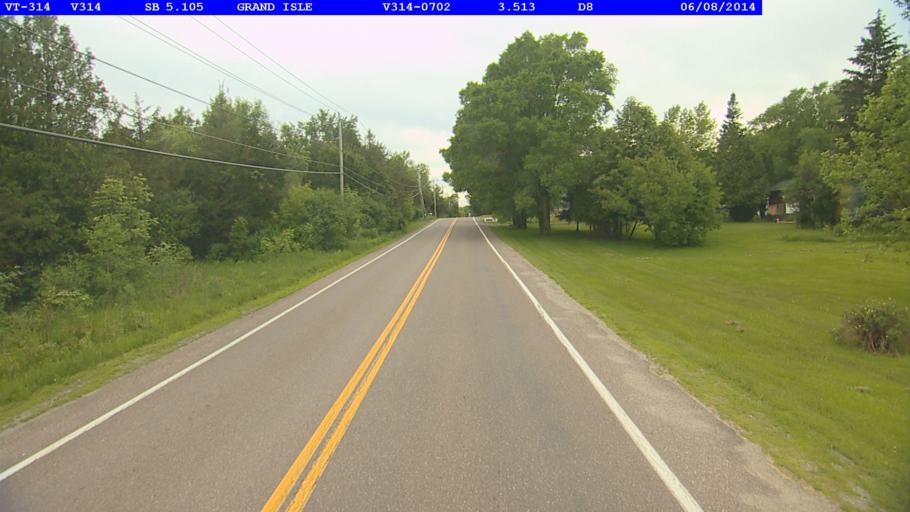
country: US
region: New York
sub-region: Clinton County
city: Cumberland Head
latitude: 44.7025
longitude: -73.3105
